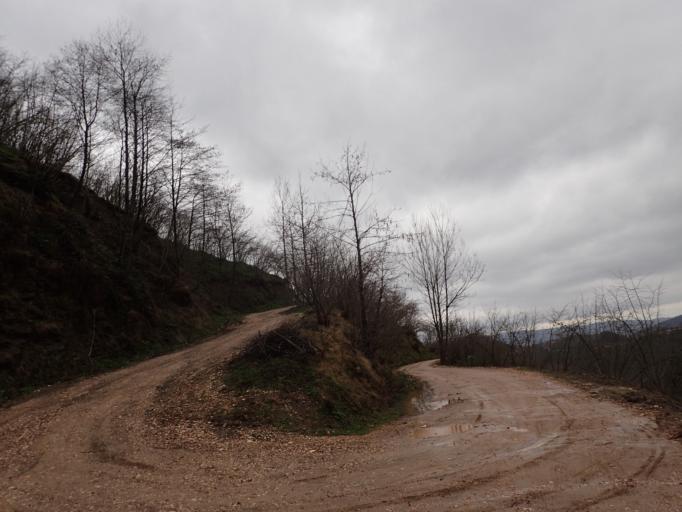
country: TR
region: Ordu
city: Camas
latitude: 40.8719
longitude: 37.5096
